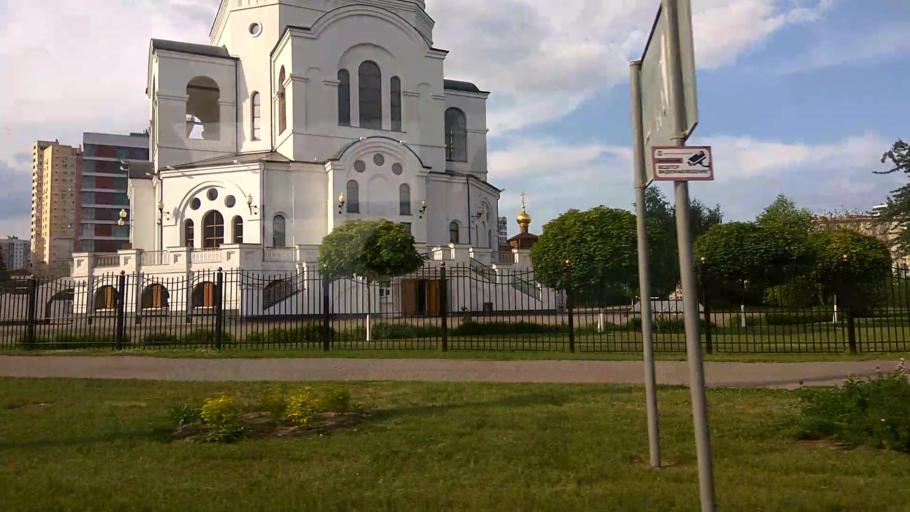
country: RU
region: Moskovskaya
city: Mytishchi
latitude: 55.9163
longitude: 37.7480
